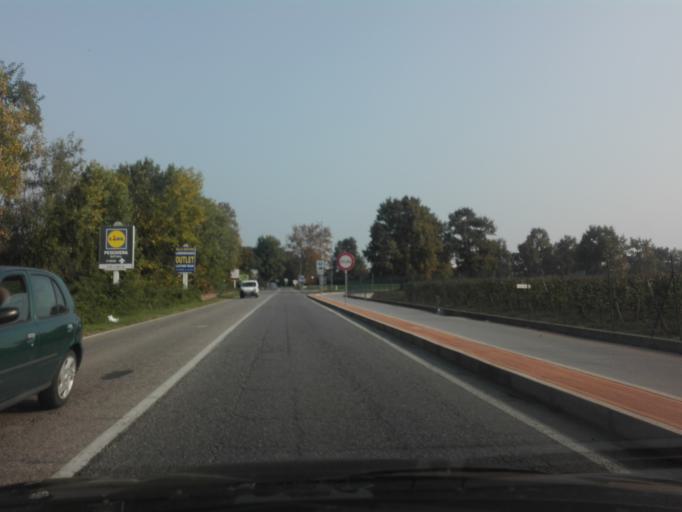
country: IT
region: Veneto
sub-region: Provincia di Verona
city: Peschiera del Garda
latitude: 45.4554
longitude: 10.6453
